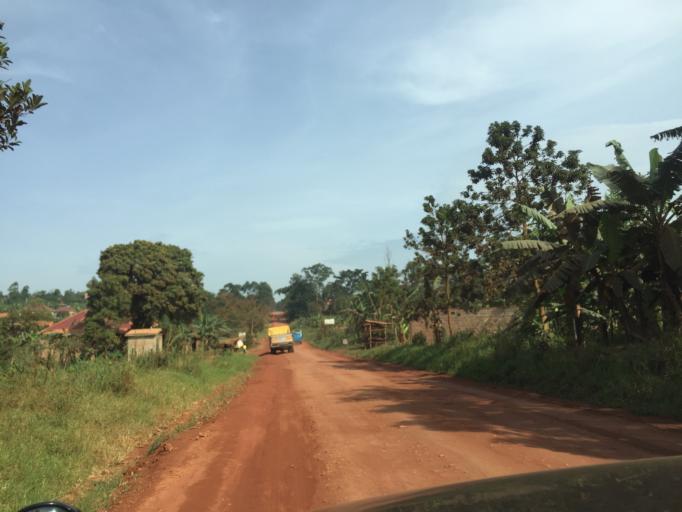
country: UG
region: Central Region
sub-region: Wakiso District
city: Wakiso
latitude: 0.4555
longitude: 32.5646
